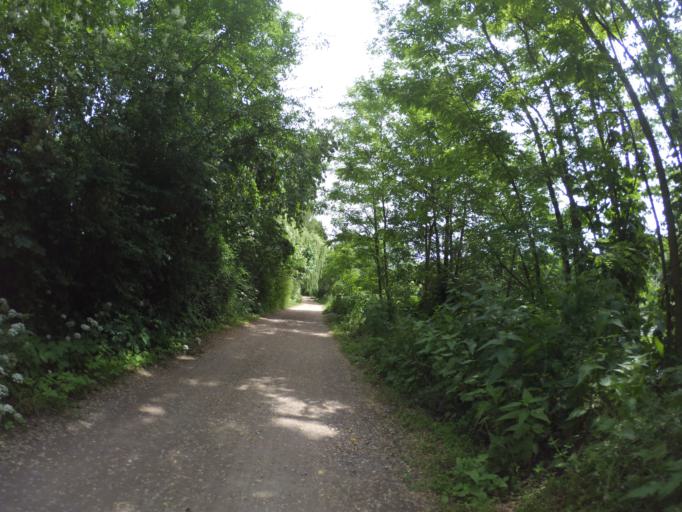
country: CZ
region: Central Bohemia
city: Prerov nad Labem
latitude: 50.1742
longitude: 14.8612
